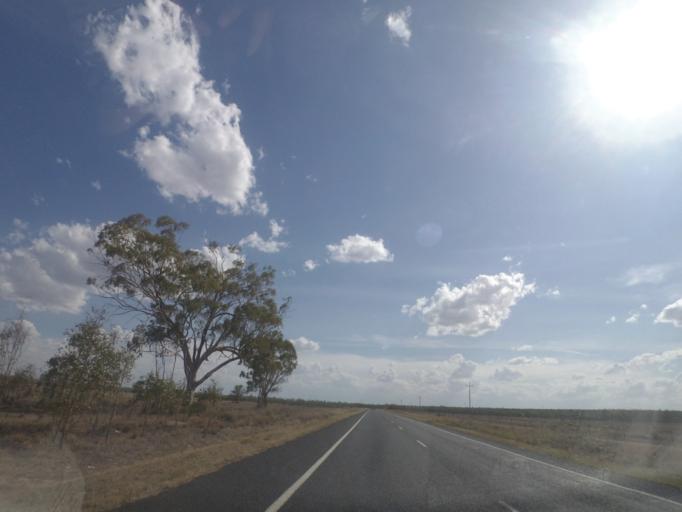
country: AU
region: New South Wales
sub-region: Moree Plains
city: Boggabilla
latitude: -28.5270
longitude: 150.9013
